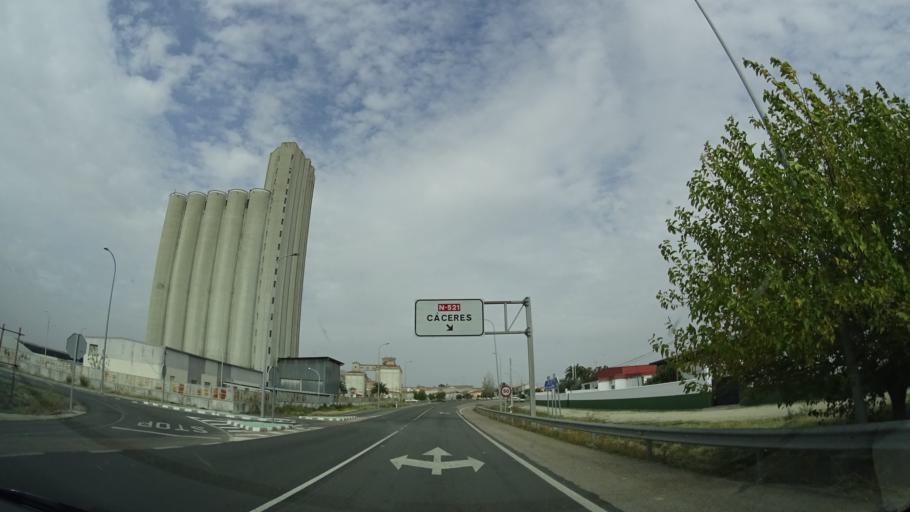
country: ES
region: Extremadura
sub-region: Provincia de Caceres
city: Trujillo
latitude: 39.4507
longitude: -5.8809
